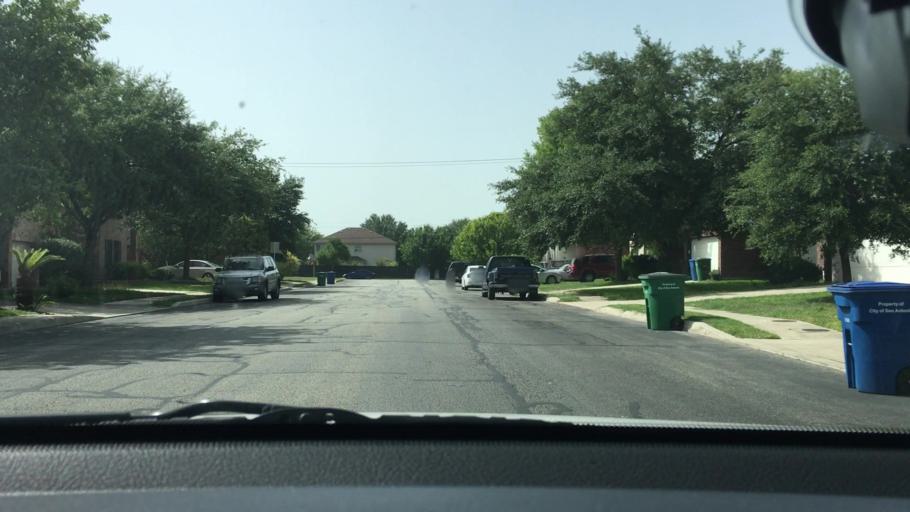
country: US
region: Texas
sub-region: Bexar County
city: Live Oak
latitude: 29.5829
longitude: -98.3833
